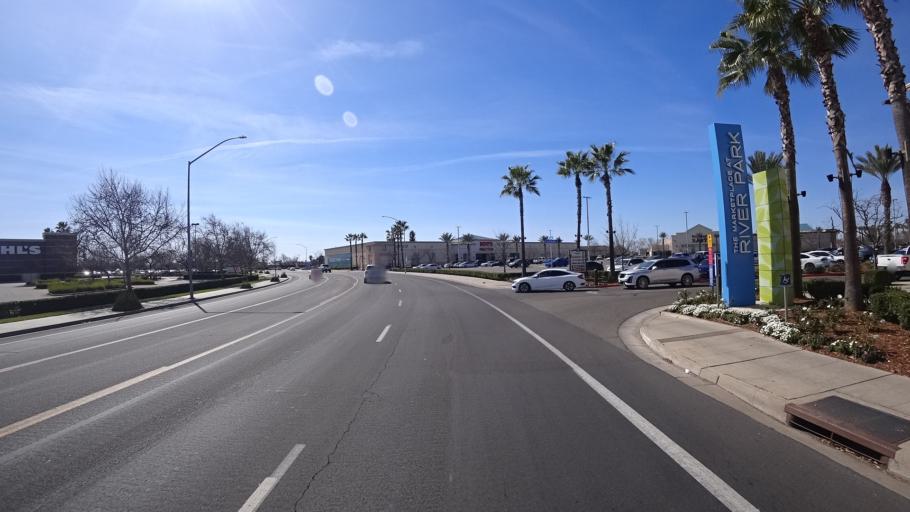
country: US
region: California
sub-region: Fresno County
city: Clovis
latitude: 36.8446
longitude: -119.7864
